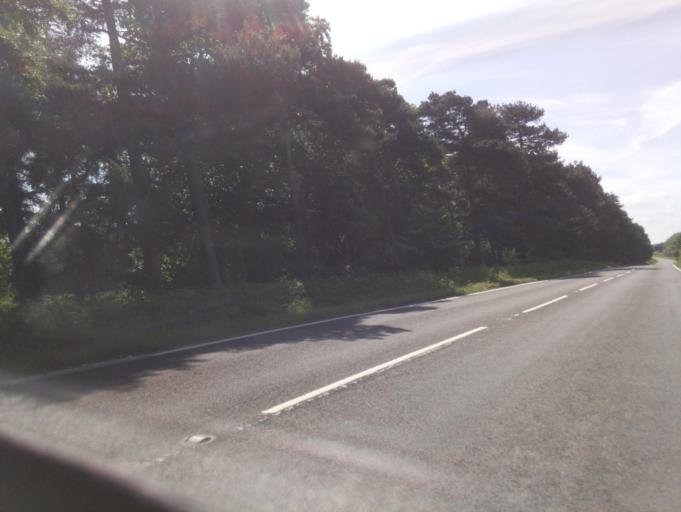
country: GB
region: England
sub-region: North Lincolnshire
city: Manton
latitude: 53.5216
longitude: -0.5799
